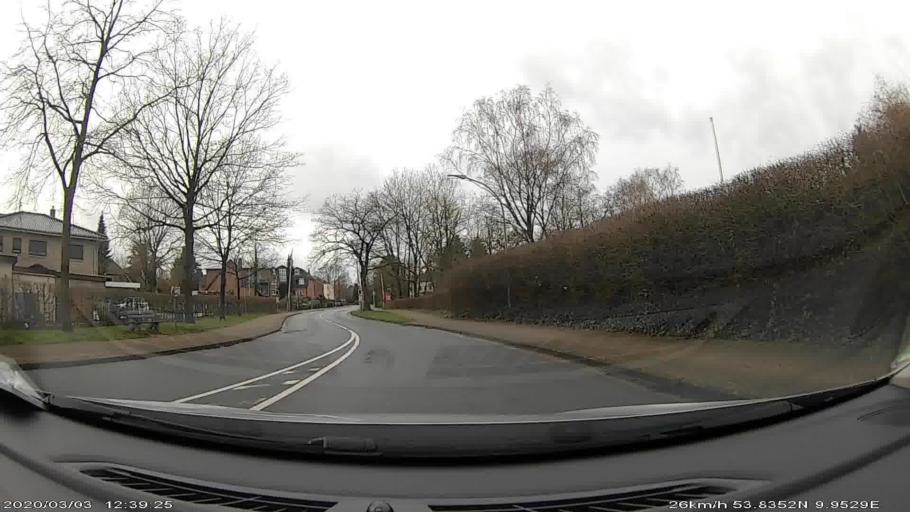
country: DE
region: Schleswig-Holstein
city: Kaltenkirchen
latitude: 53.8352
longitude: 9.9512
